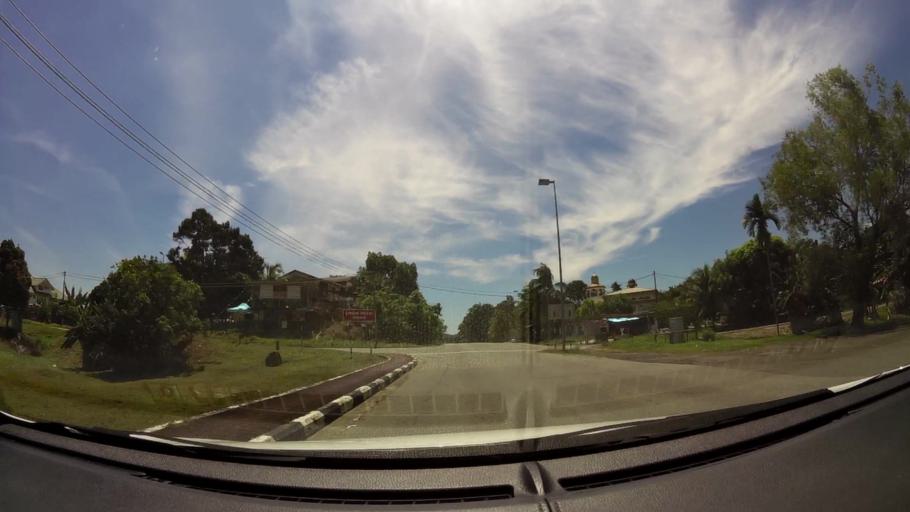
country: BN
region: Brunei and Muara
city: Bandar Seri Begawan
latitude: 4.9336
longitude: 114.9507
